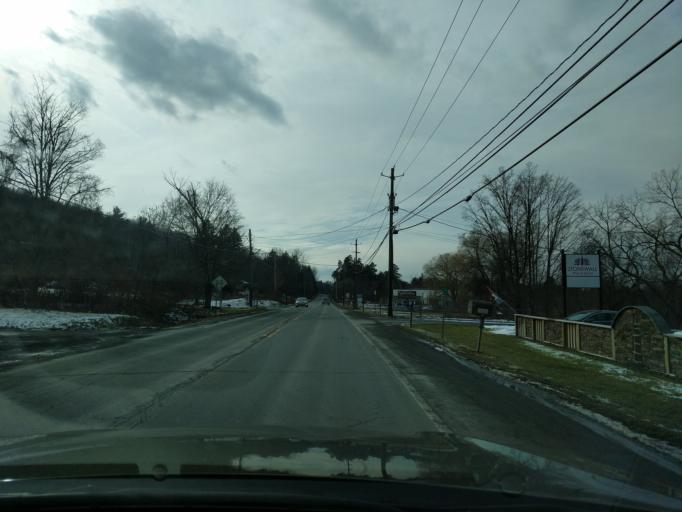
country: US
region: New York
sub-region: Tompkins County
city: Northeast Ithaca
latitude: 42.4674
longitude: -76.4110
